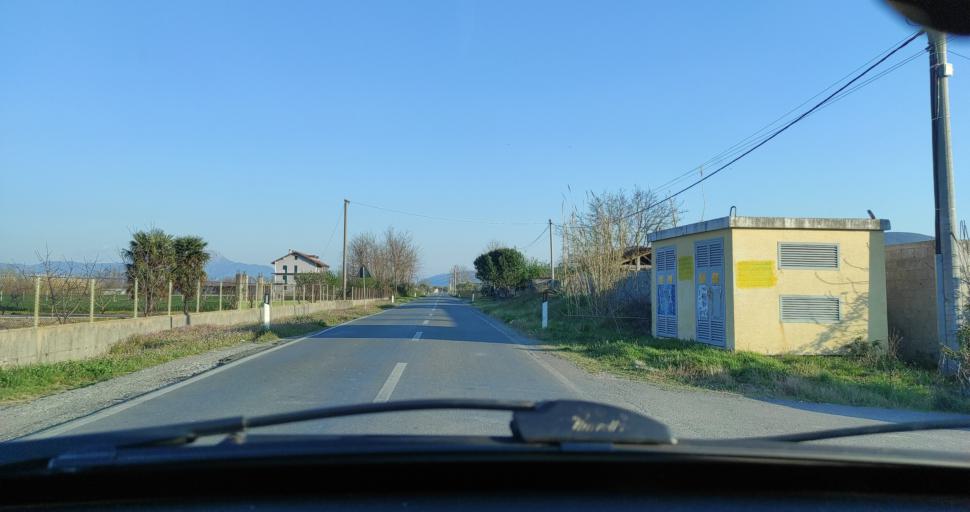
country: AL
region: Shkoder
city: Vukatane
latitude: 41.9494
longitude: 19.5310
